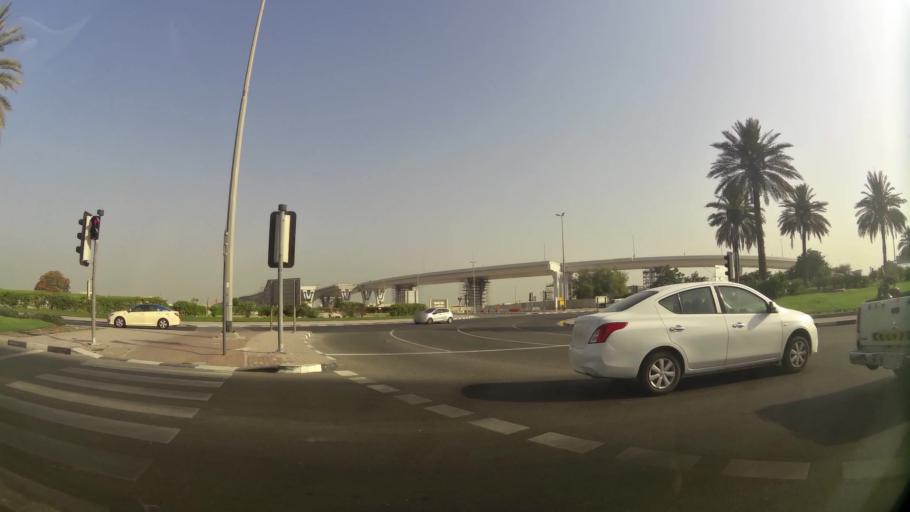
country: AE
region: Ash Shariqah
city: Sharjah
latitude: 25.2873
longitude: 55.3220
